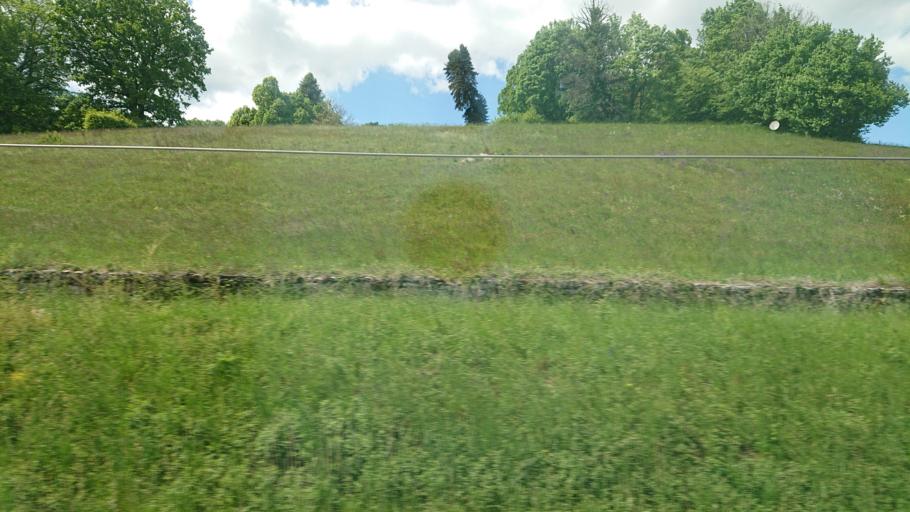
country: CH
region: Vaud
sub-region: Nyon District
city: Founex
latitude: 46.3531
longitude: 6.2059
